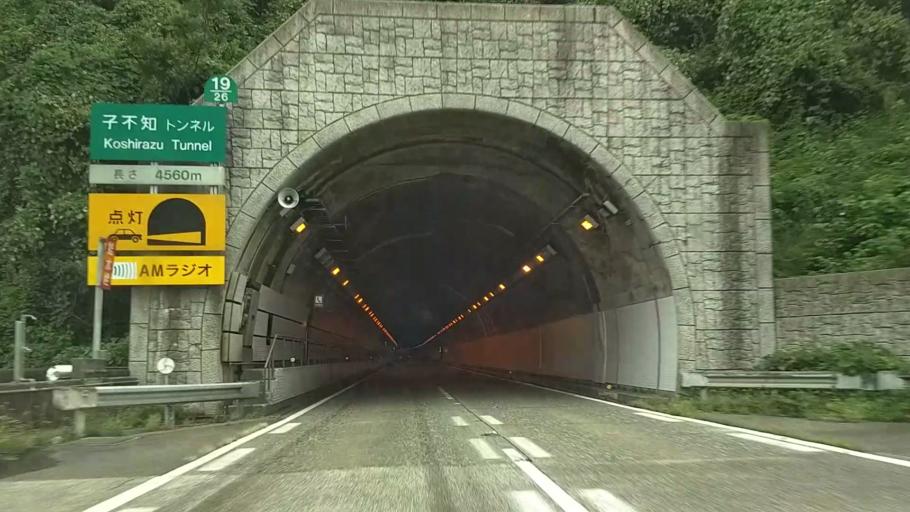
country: JP
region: Niigata
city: Itoigawa
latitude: 37.0179
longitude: 137.7911
